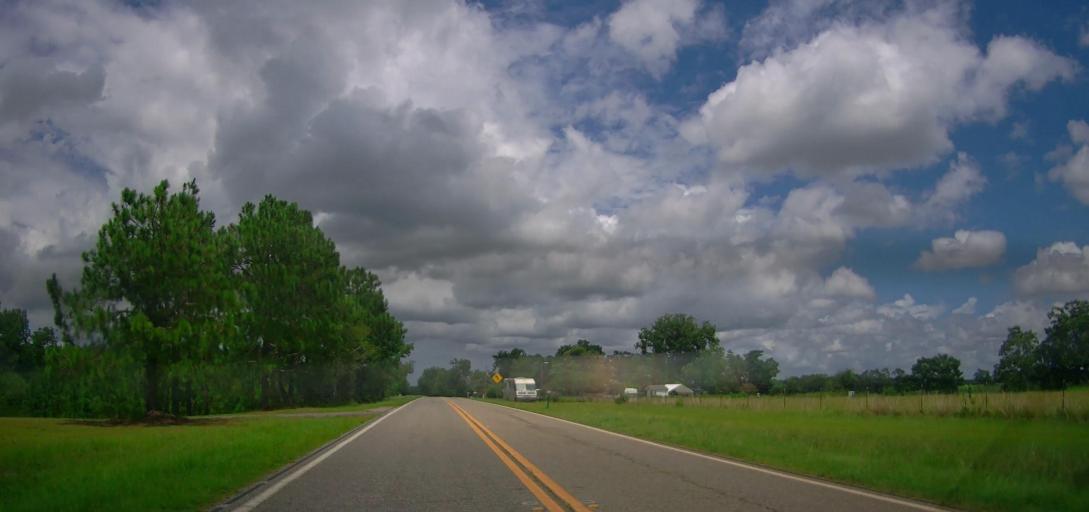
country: US
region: Georgia
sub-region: Wilcox County
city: Rochelle
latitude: 31.8916
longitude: -83.5540
